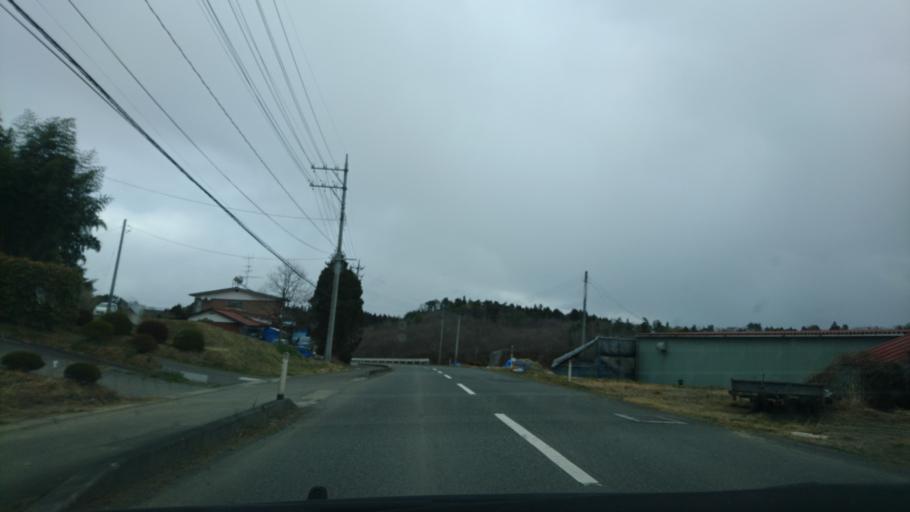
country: JP
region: Iwate
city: Ichinoseki
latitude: 38.8251
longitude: 141.1723
